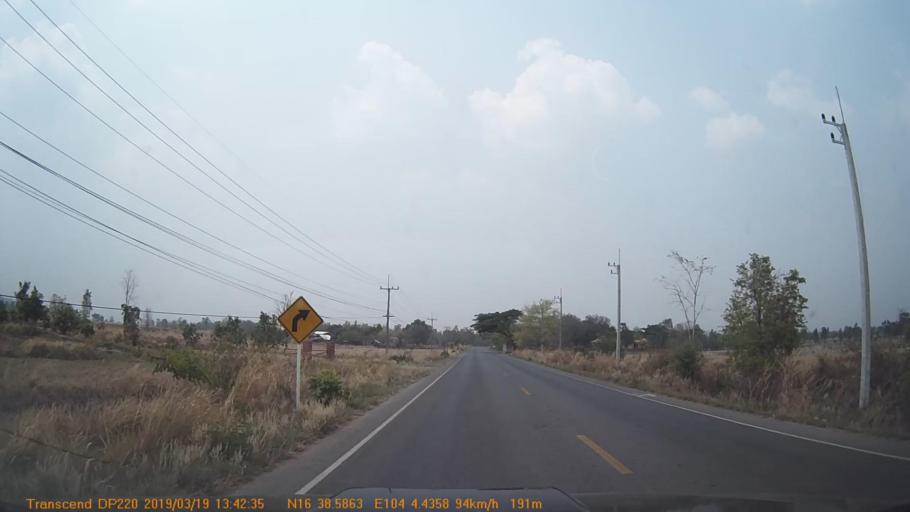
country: TH
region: Kalasin
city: Khao Wong
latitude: 16.6437
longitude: 104.0737
